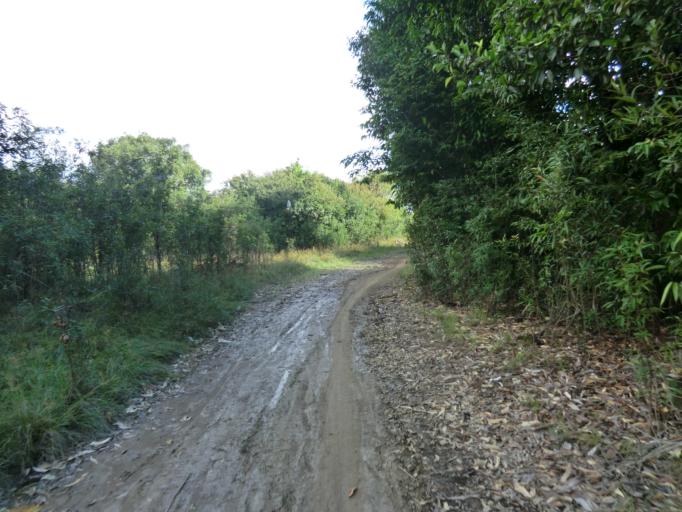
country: MY
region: Sarawak
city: Simanggang
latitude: 1.0292
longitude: 112.2252
